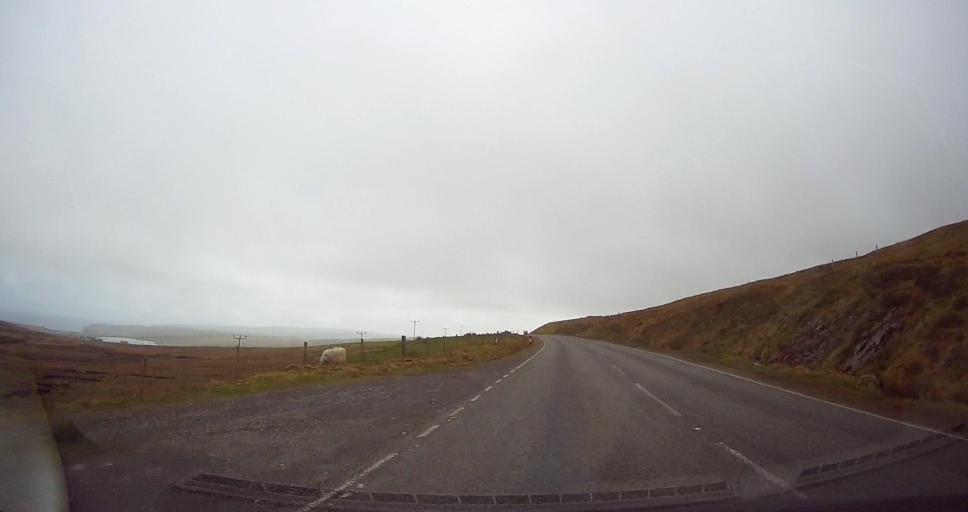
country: GB
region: Scotland
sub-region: Shetland Islands
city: Sandwick
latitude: 59.9593
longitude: -1.2846
